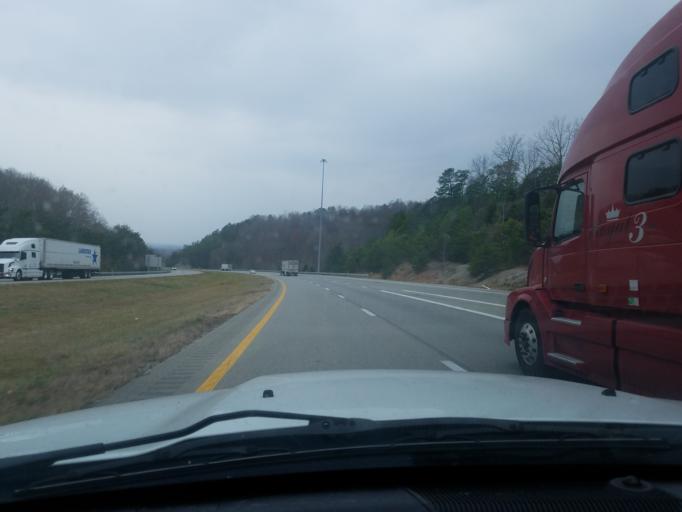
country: US
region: Kentucky
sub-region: Rowan County
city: Morehead
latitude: 38.1822
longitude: -83.5630
